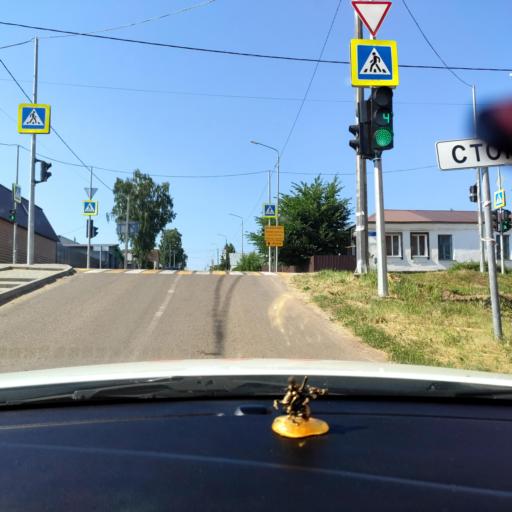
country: RU
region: Tatarstan
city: Laishevo
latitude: 55.4064
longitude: 49.5428
